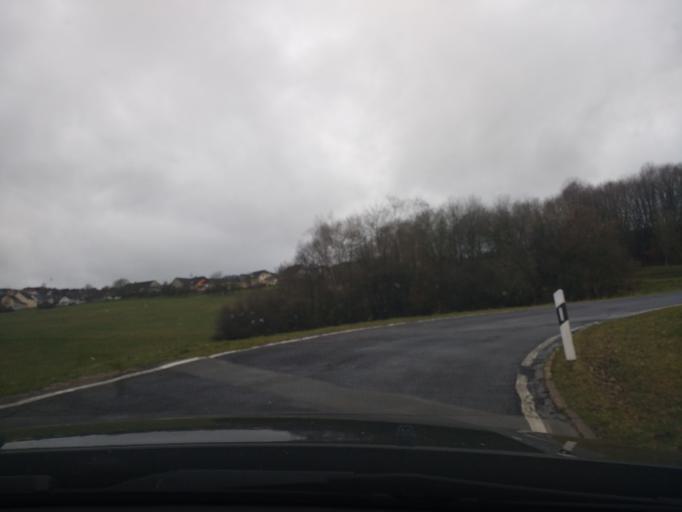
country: DE
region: Rheinland-Pfalz
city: Baldringen
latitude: 49.6146
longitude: 6.6914
